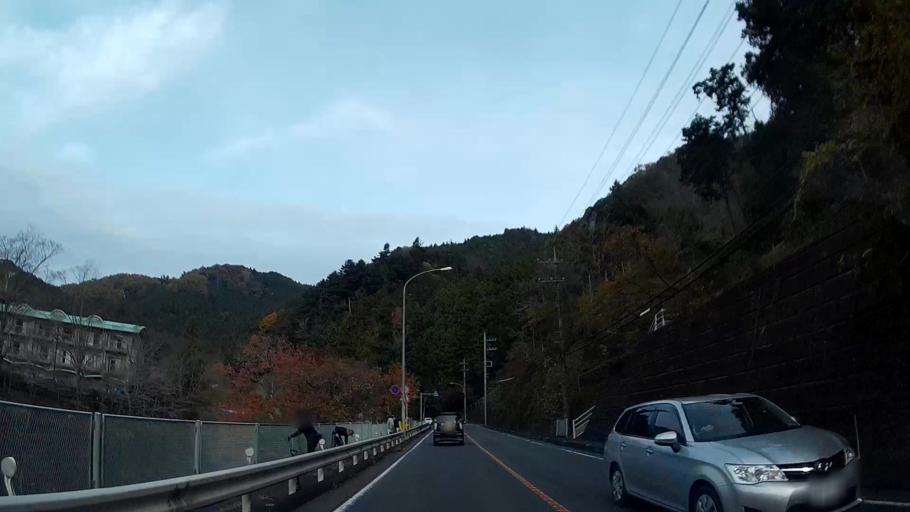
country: JP
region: Saitama
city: Morohongo
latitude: 35.9207
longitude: 139.2109
